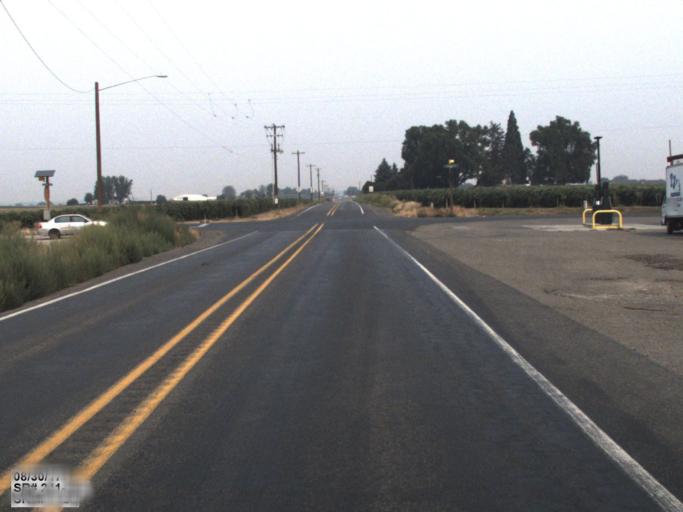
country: US
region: Washington
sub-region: Yakima County
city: Sunnyside
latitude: 46.3311
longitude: -119.9790
